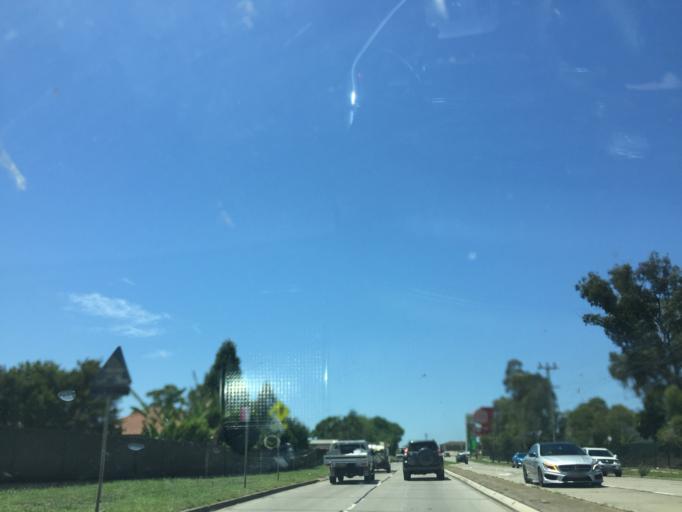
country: AU
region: New South Wales
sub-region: Blacktown
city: Glendenning
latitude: -33.7356
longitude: 150.8518
